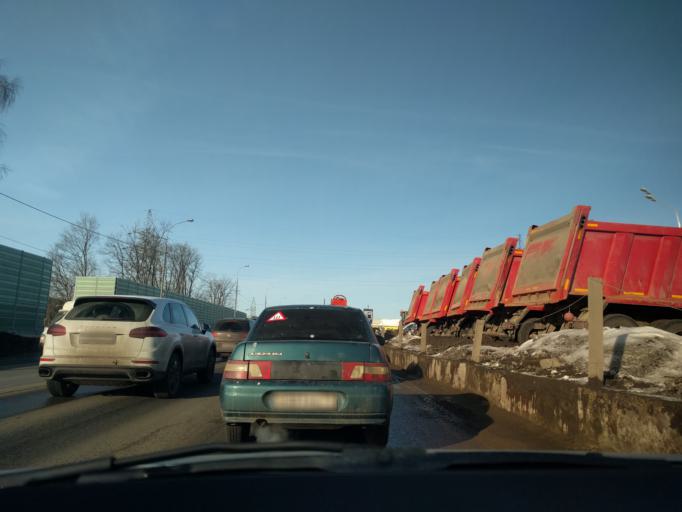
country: RU
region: Moskovskaya
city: Sheremet'yevskiy
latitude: 55.9881
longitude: 37.5309
